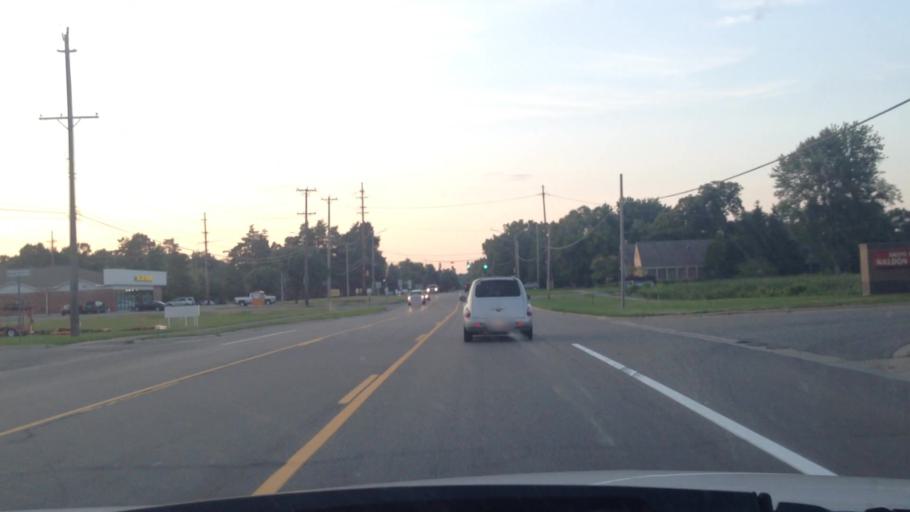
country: US
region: Michigan
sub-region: Oakland County
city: Lake Orion
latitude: 42.7343
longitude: -83.3079
